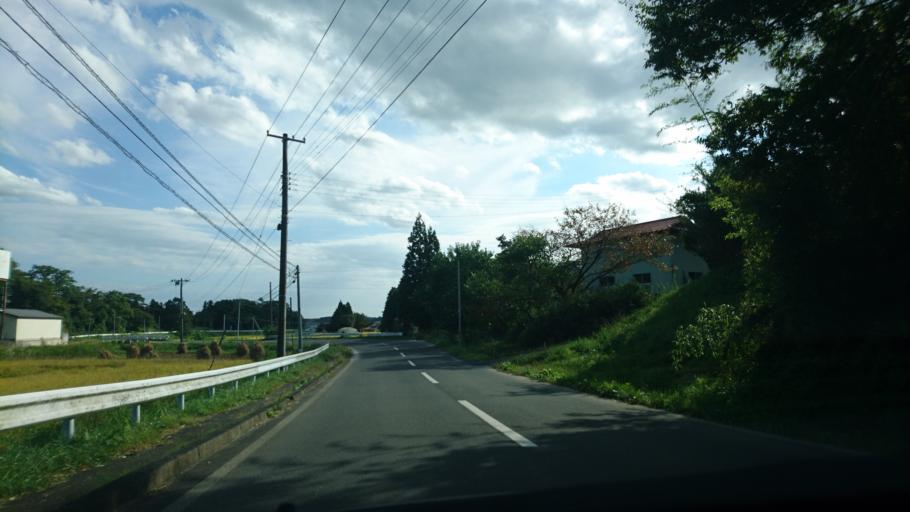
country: JP
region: Iwate
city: Ichinoseki
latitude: 38.8394
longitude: 141.1916
